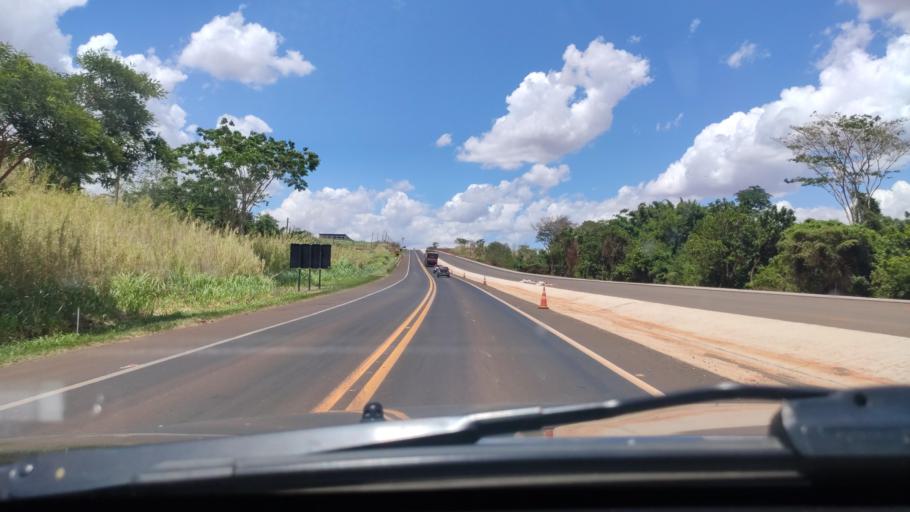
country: BR
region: Sao Paulo
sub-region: Jau
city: Jau
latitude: -22.2346
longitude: -48.5349
